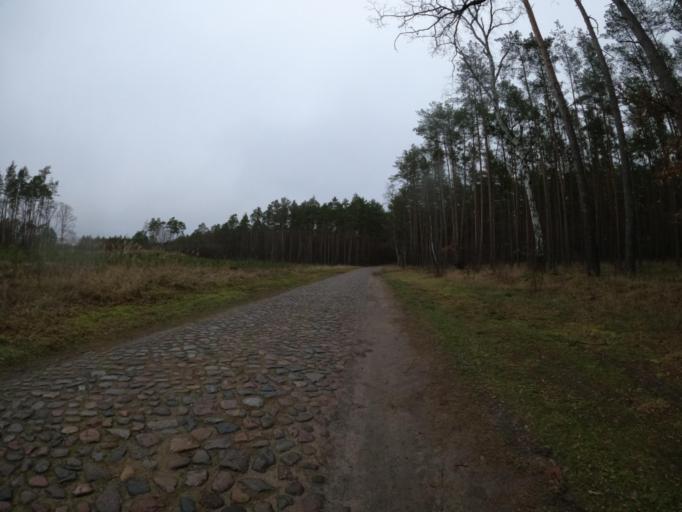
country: PL
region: West Pomeranian Voivodeship
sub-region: Powiat mysliborski
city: Debno
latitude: 52.7132
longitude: 14.7240
